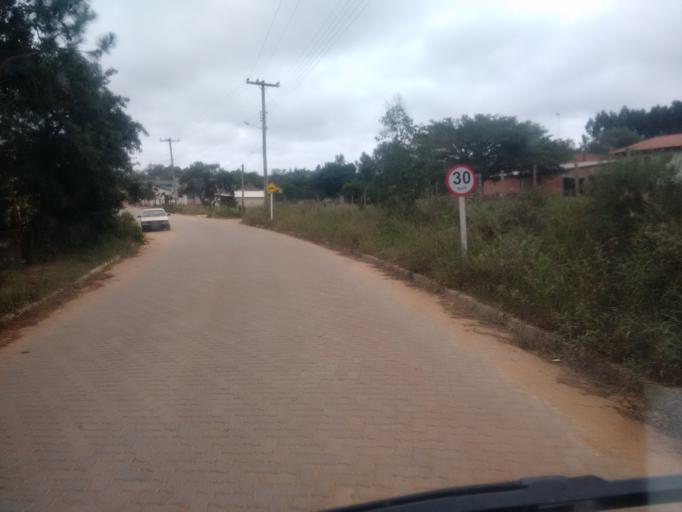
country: BR
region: Rio Grande do Sul
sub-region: Camaqua
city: Camaqua
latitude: -30.7897
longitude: -51.8325
